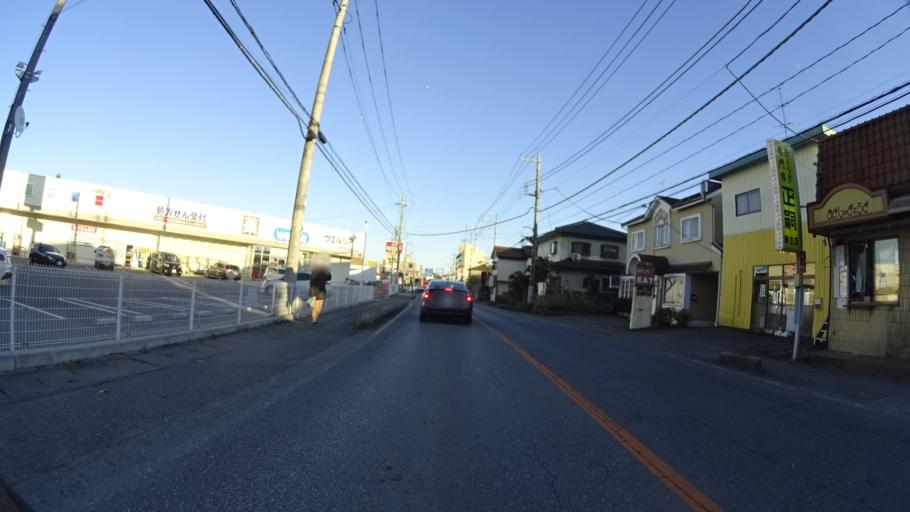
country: JP
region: Tochigi
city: Utsunomiya-shi
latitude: 36.5788
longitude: 139.8438
